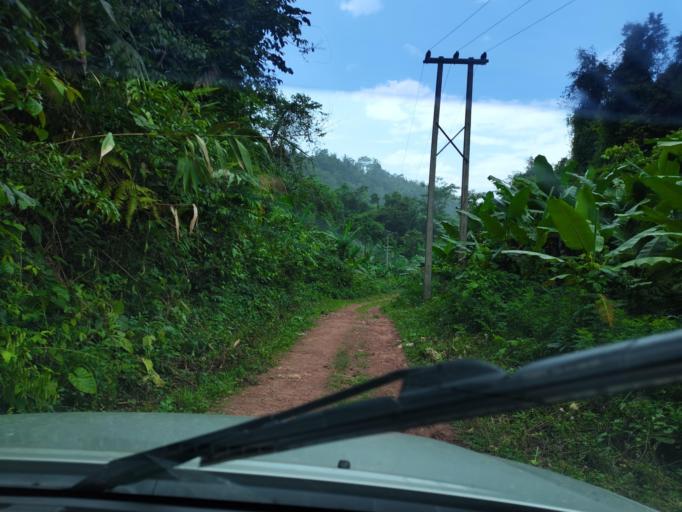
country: LA
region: Loungnamtha
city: Muang Nale
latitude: 20.5171
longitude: 101.0708
